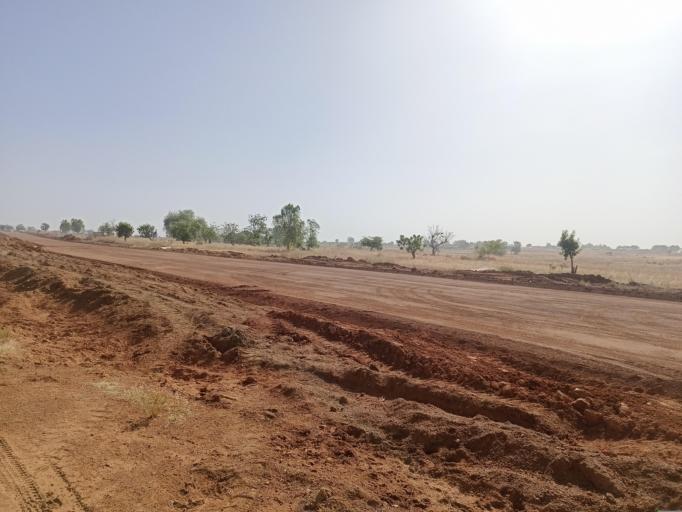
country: BF
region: Centre-Est
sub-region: Province du Boulgou
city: Tenkodogo
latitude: 11.5327
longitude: -0.4839
